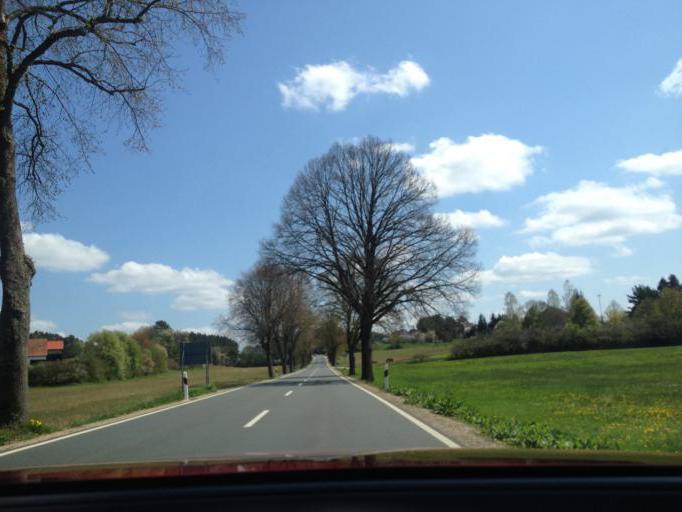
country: DE
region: Bavaria
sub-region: Upper Franconia
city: Pottenstein
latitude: 49.7287
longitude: 11.4647
